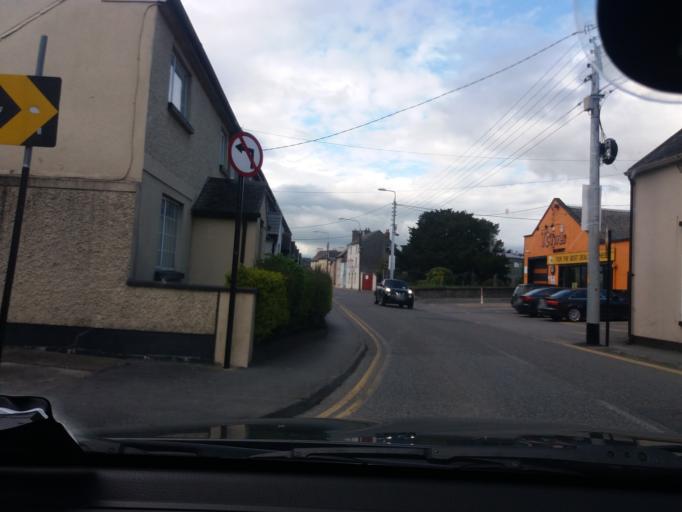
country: IE
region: Leinster
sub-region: Kilkenny
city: Kilkenny
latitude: 52.6471
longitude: -7.2507
